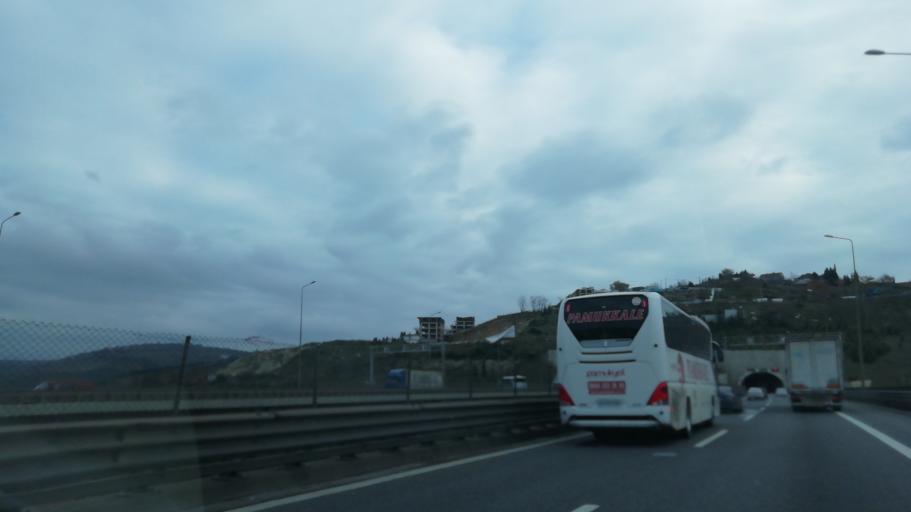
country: TR
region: Kocaeli
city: Izmit
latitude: 40.7751
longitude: 29.9023
